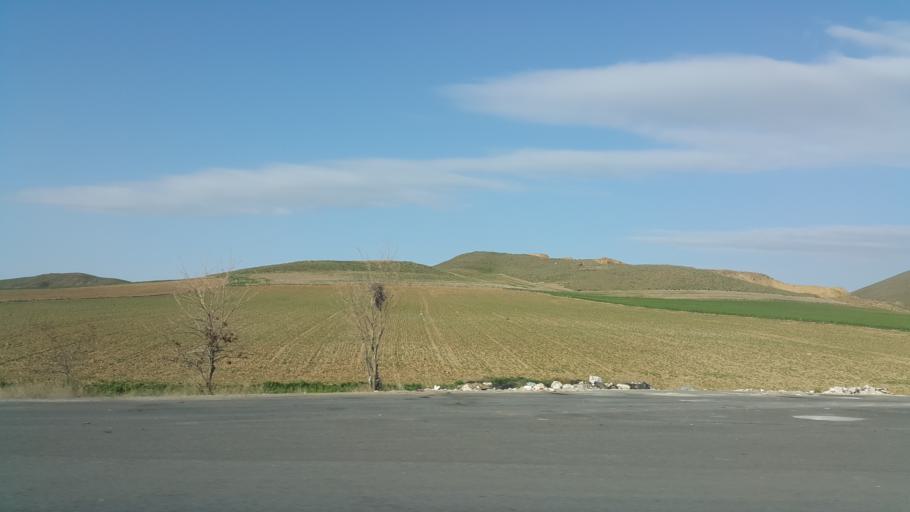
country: TR
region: Ankara
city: Sereflikochisar
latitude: 39.0845
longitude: 33.4024
